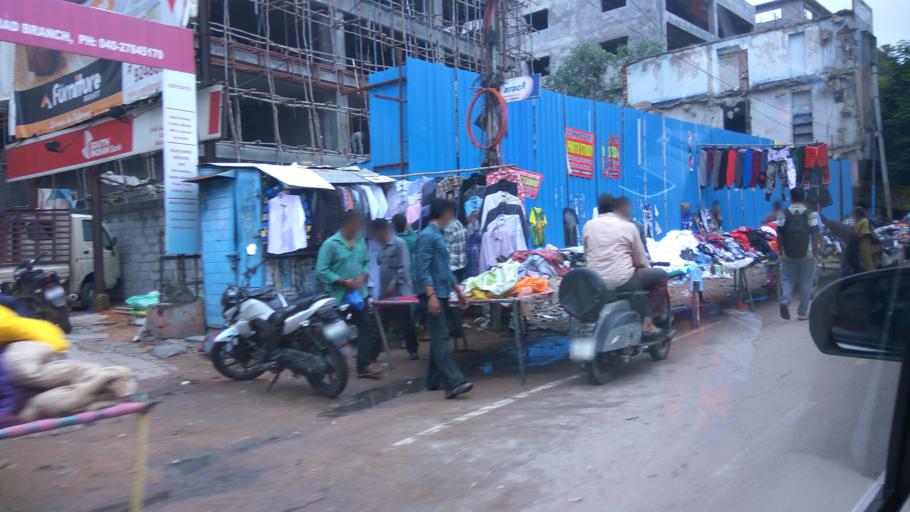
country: IN
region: Telangana
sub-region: Hyderabad
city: Malkajgiri
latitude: 17.4420
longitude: 78.4889
